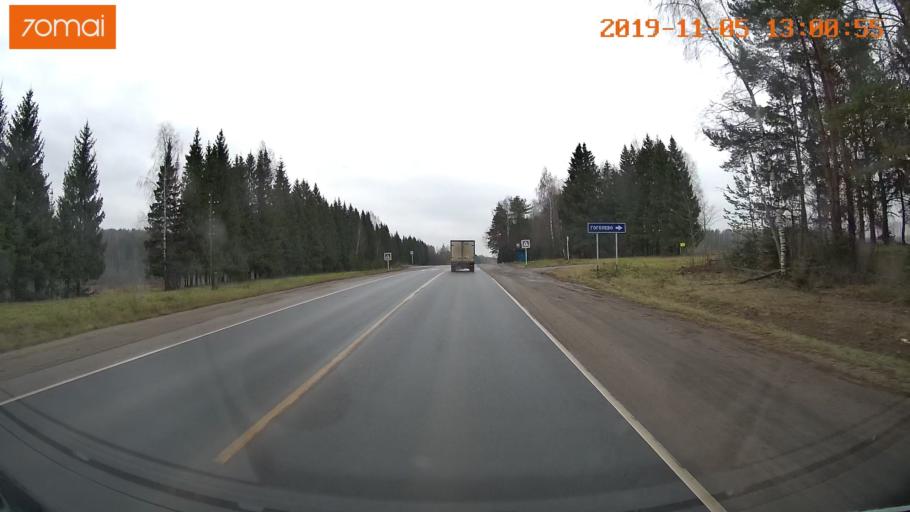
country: RU
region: Ivanovo
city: Kokhma
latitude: 56.9113
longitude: 41.1541
